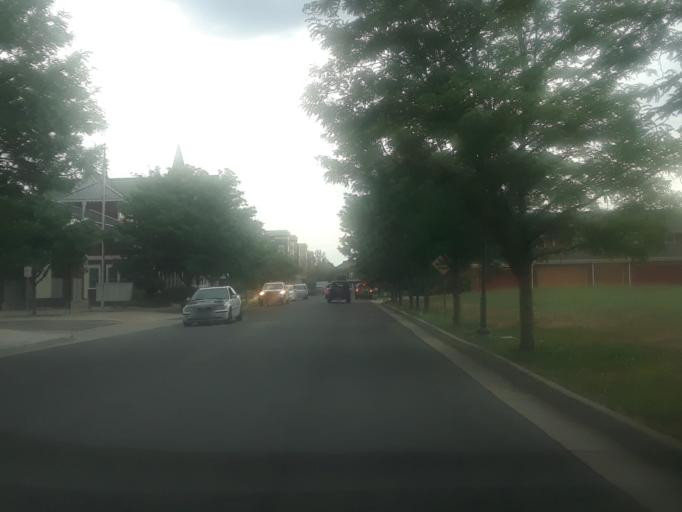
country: US
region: Colorado
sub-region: Broomfield County
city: Broomfield
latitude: 39.9129
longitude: -105.0415
